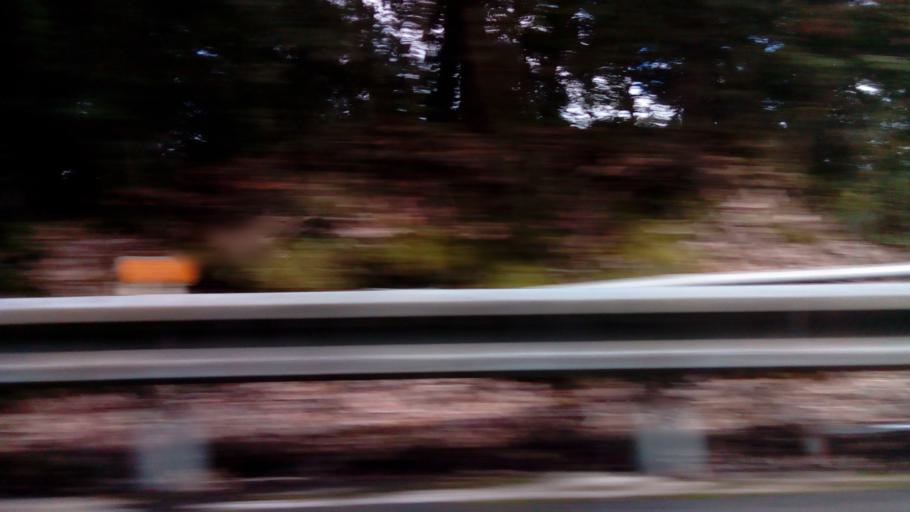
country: TW
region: Taiwan
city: Daxi
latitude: 24.4055
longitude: 121.3636
